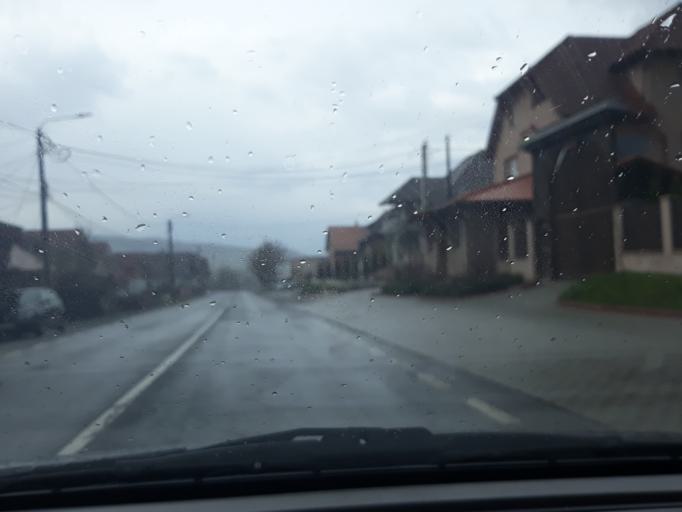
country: RO
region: Harghita
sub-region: Comuna Corund
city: Corund
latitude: 46.4778
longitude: 25.1752
